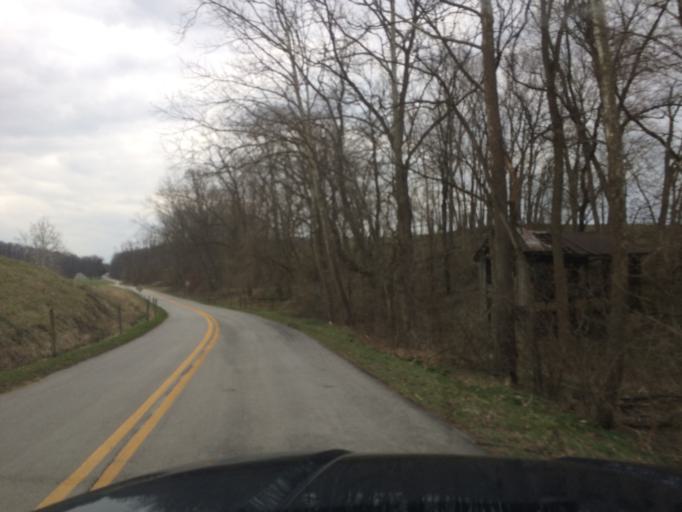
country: US
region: Maryland
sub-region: Carroll County
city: New Windsor
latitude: 39.5313
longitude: -77.1509
